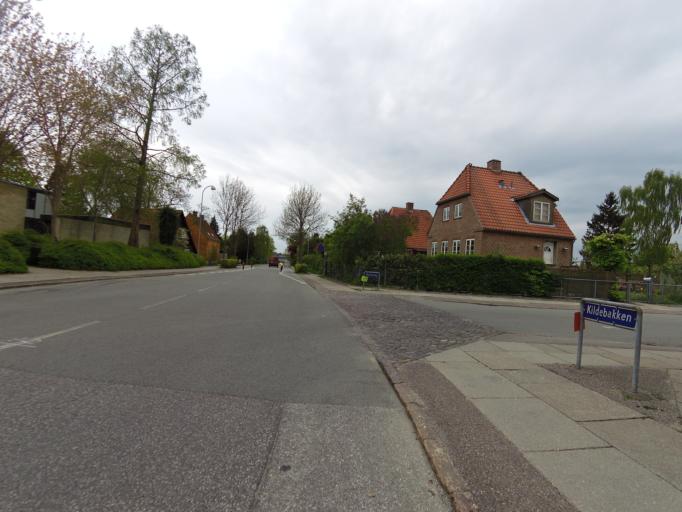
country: DK
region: Capital Region
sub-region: Gladsaxe Municipality
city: Buddinge
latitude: 55.7443
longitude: 12.4989
